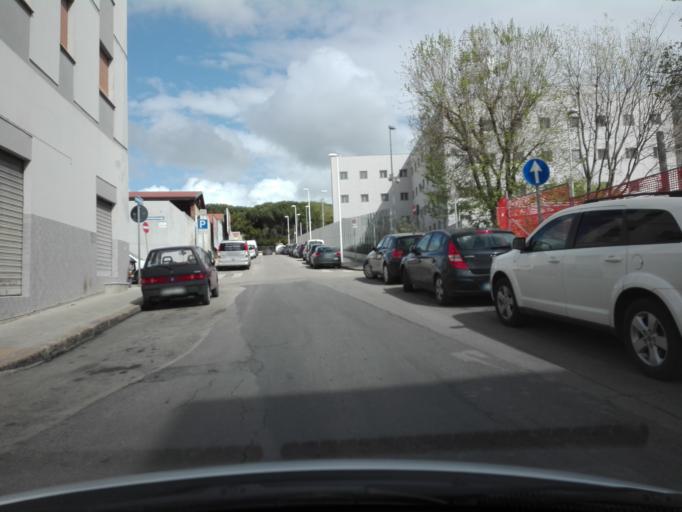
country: IT
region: Sardinia
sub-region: Provincia di Sassari
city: Sassari
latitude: 40.7364
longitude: 8.5624
